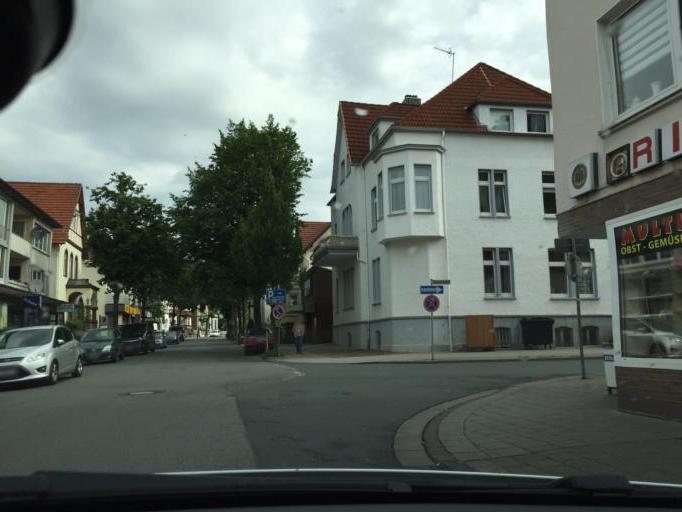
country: DE
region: Lower Saxony
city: Bad Pyrmont
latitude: 51.9832
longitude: 9.2598
